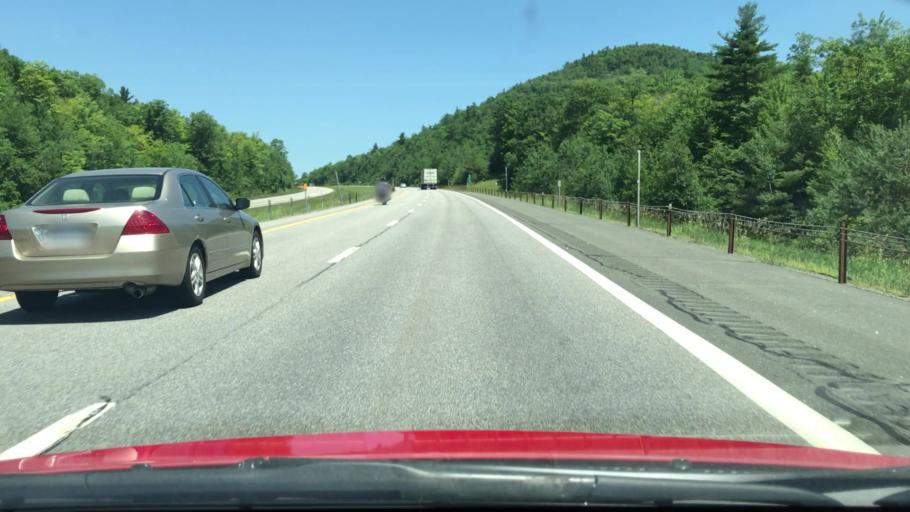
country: US
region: New York
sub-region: Essex County
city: Keeseville
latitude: 44.3895
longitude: -73.5042
